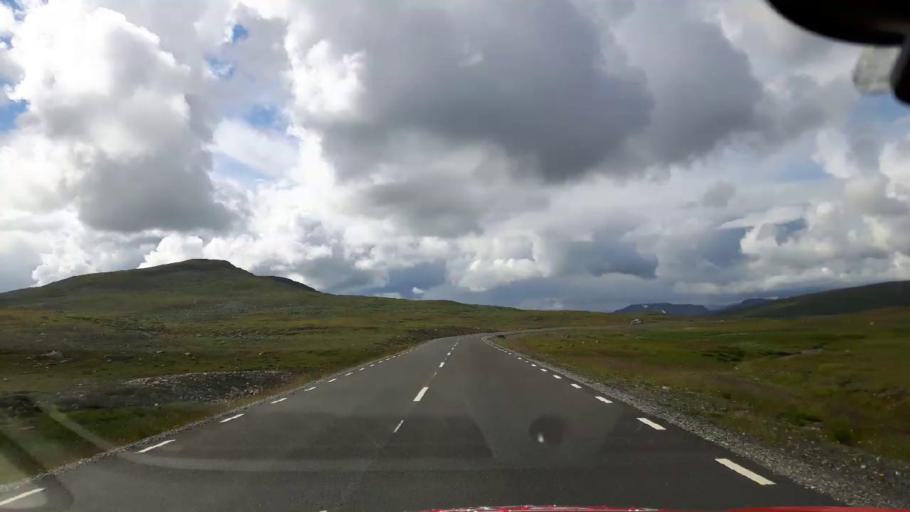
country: NO
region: Nordland
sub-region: Hattfjelldal
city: Hattfjelldal
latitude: 65.0601
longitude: 14.3737
